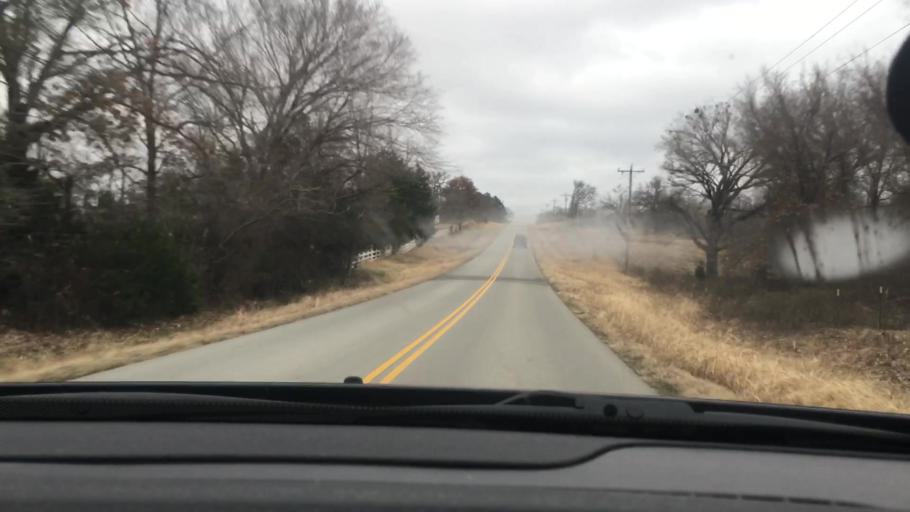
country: US
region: Oklahoma
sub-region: Atoka County
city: Atoka
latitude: 34.3252
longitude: -96.0755
